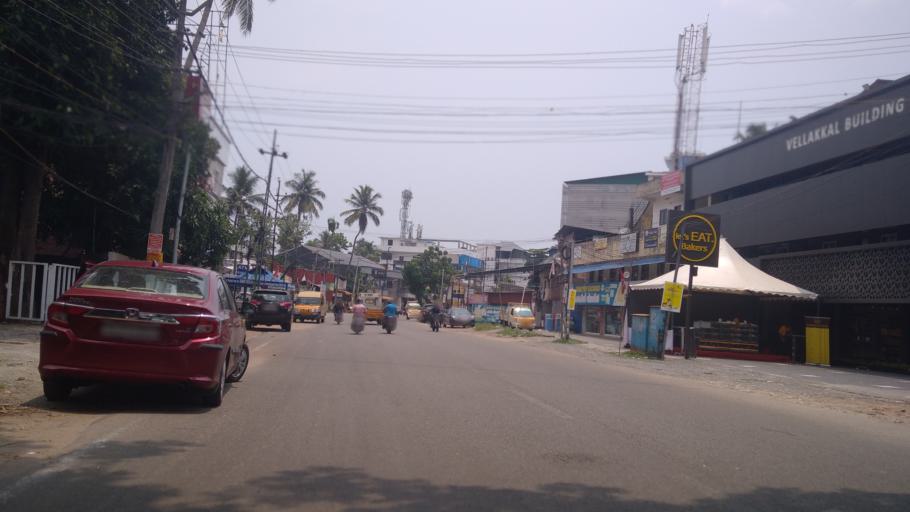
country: IN
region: Kerala
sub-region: Ernakulam
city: Elur
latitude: 10.0304
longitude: 76.3202
